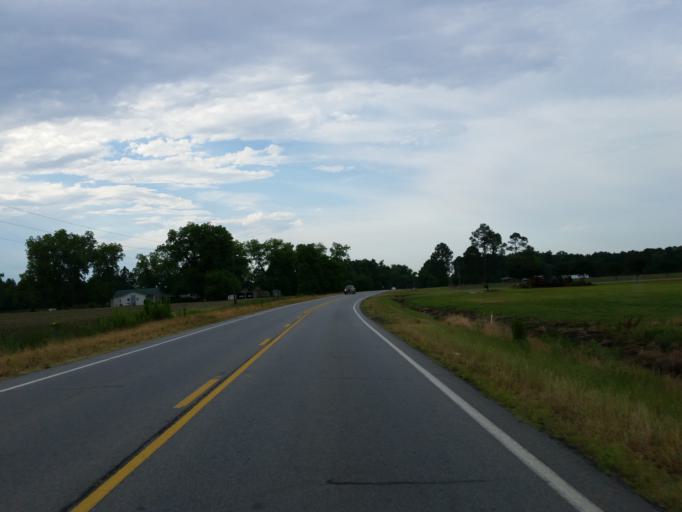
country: US
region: Georgia
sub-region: Dooly County
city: Vienna
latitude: 32.0475
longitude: -83.7965
